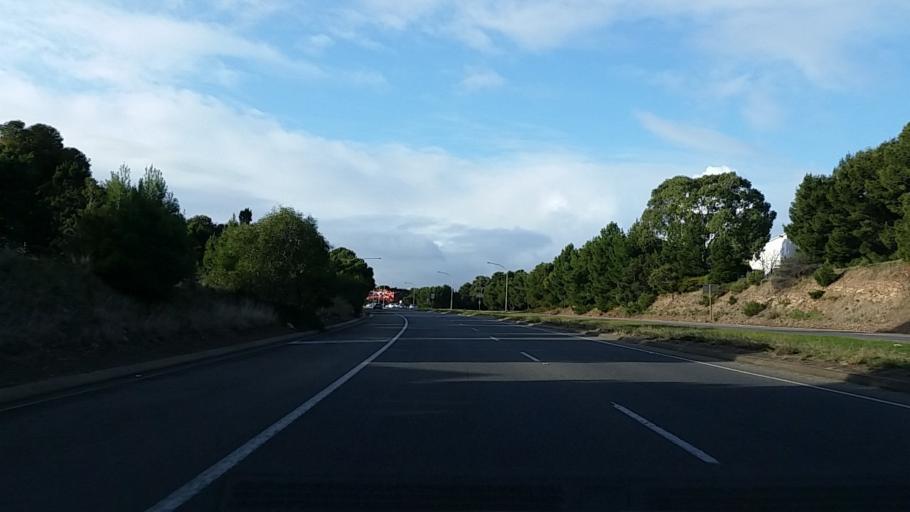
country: AU
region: South Australia
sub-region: Onkaparinga
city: Morphett Vale
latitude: -35.1087
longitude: 138.4968
